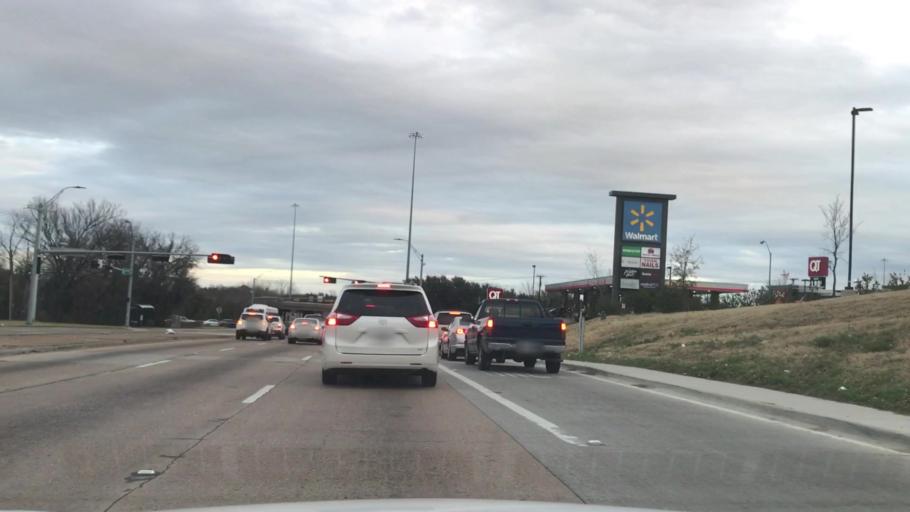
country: US
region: Texas
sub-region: Dallas County
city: Cockrell Hill
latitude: 32.6879
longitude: -96.8264
